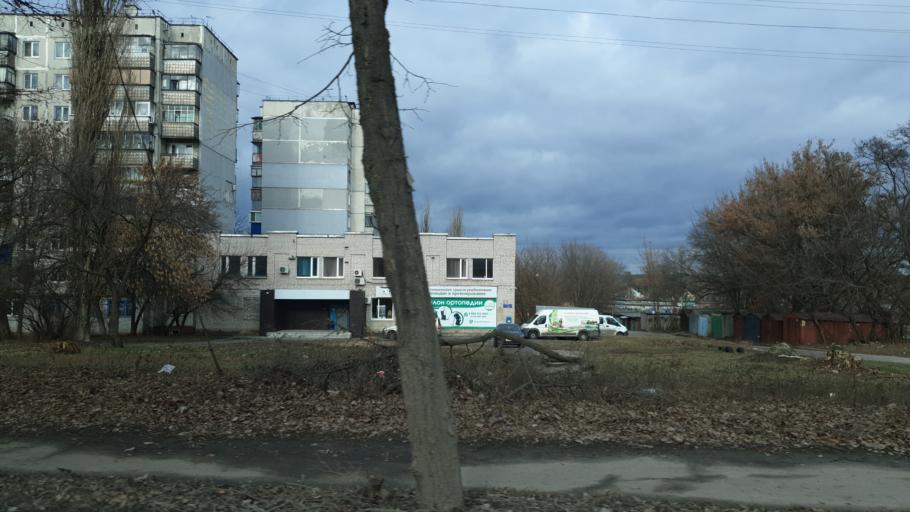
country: RU
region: Kursk
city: Voroshnevo
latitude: 51.6665
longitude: 36.1073
